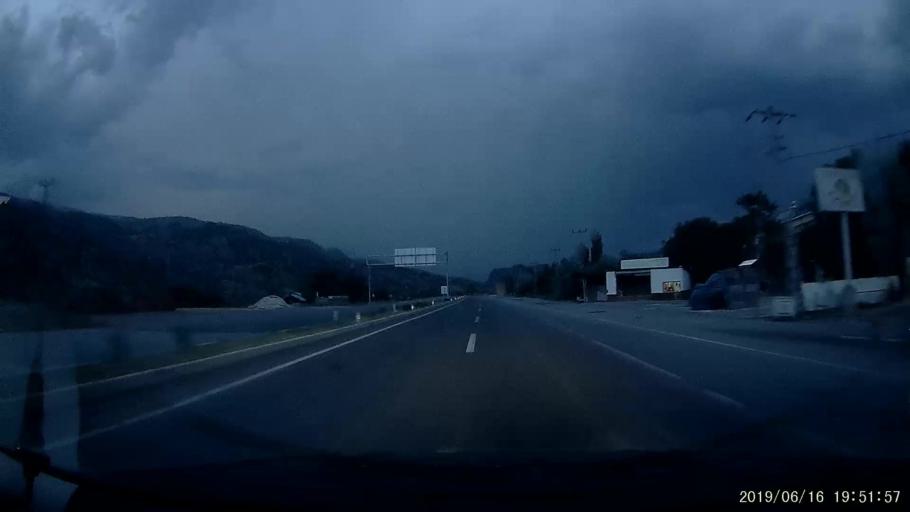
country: TR
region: Sivas
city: Koyulhisar
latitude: 40.2849
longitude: 37.8122
